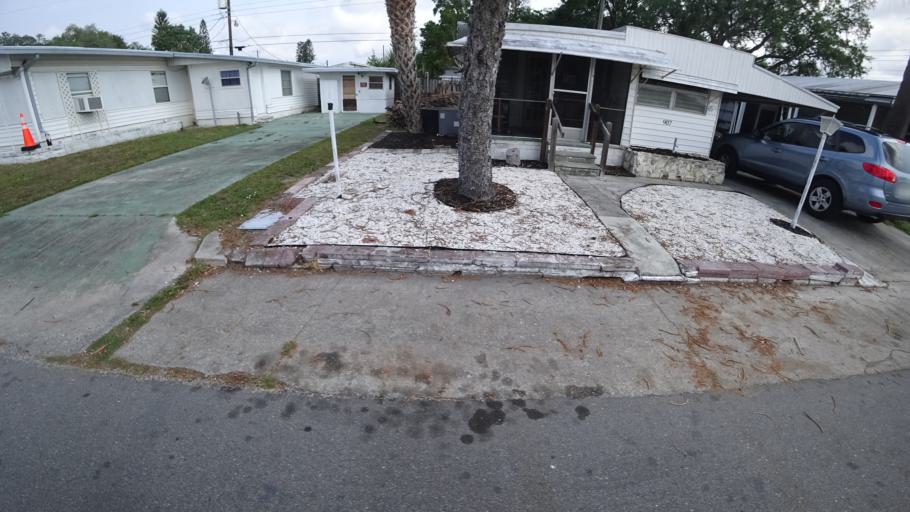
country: US
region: Florida
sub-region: Manatee County
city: South Bradenton
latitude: 27.4517
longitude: -82.5716
